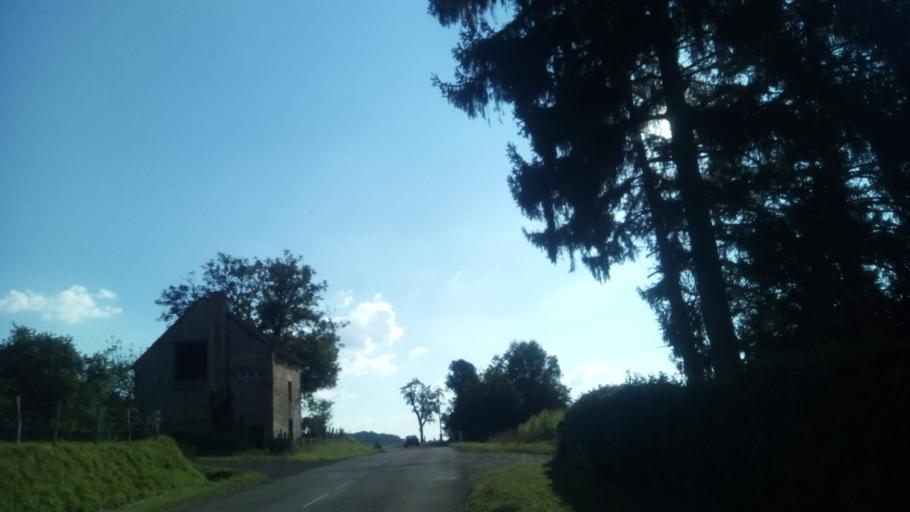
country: FR
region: Franche-Comte
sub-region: Departement de la Haute-Saone
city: Gy
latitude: 47.4210
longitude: 5.8368
